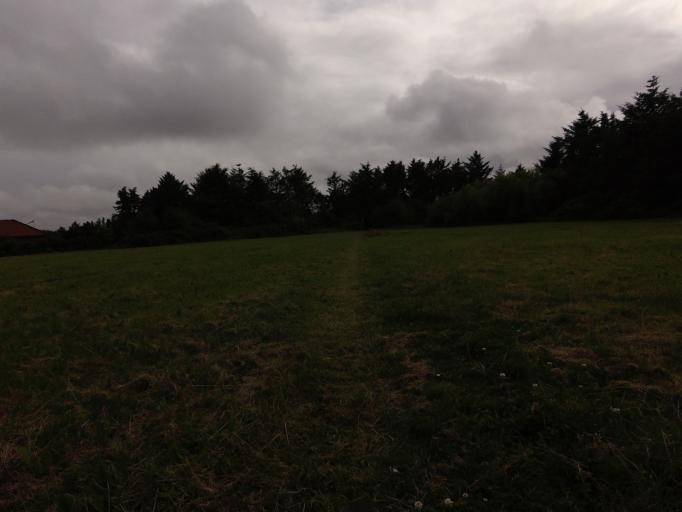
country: DK
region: North Denmark
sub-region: Jammerbugt Kommune
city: Pandrup
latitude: 57.3683
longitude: 9.7257
